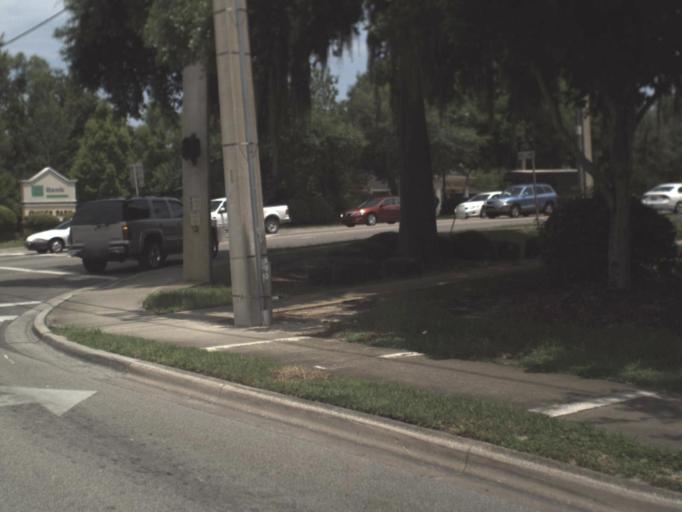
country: US
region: Florida
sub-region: Alachua County
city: Gainesville
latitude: 29.6557
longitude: -82.3900
